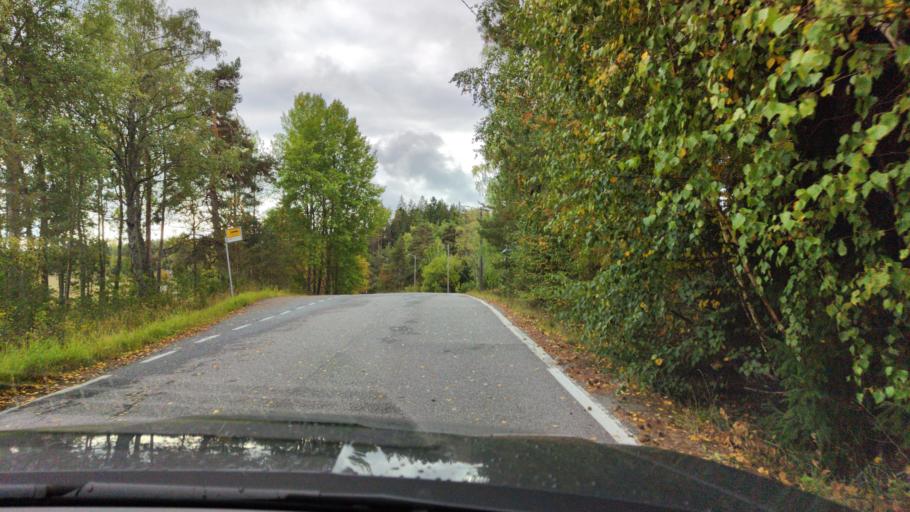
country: FI
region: Varsinais-Suomi
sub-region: Aboland-Turunmaa
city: Pargas
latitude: 60.3701
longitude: 22.2766
